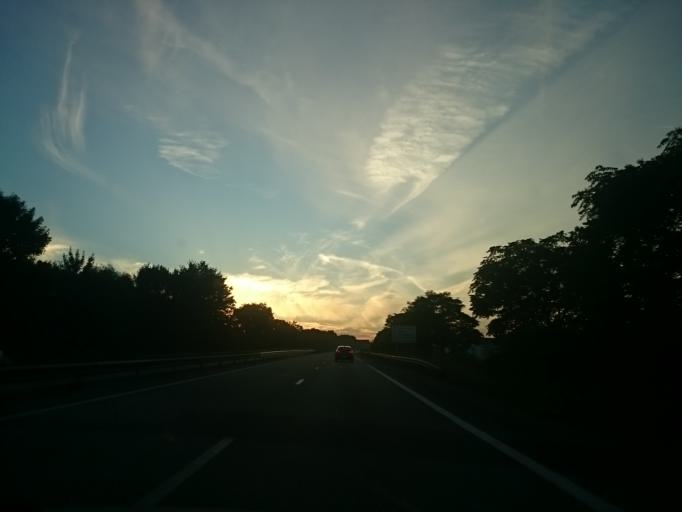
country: FR
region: Brittany
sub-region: Departement du Finistere
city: Ergue-Gaberic
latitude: 47.9709
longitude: -3.9984
